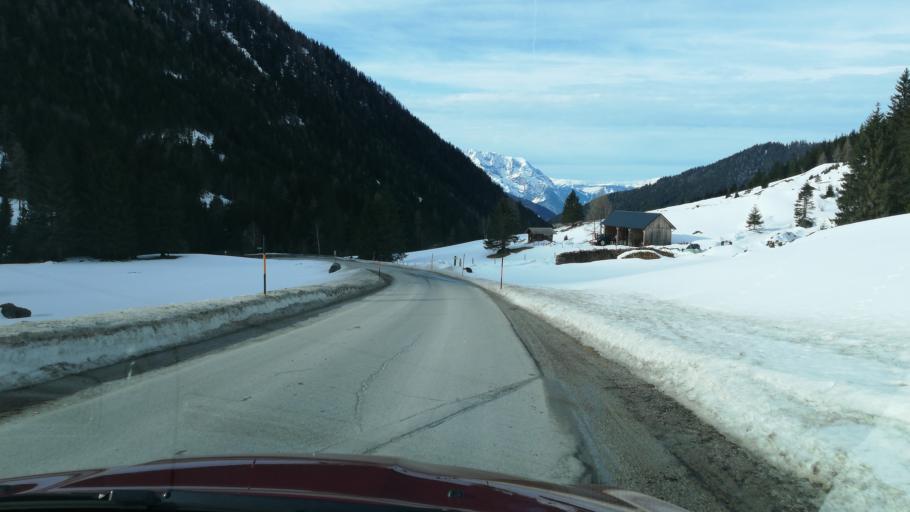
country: AT
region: Styria
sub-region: Politischer Bezirk Liezen
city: Donnersbach
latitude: 47.4170
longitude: 14.1751
